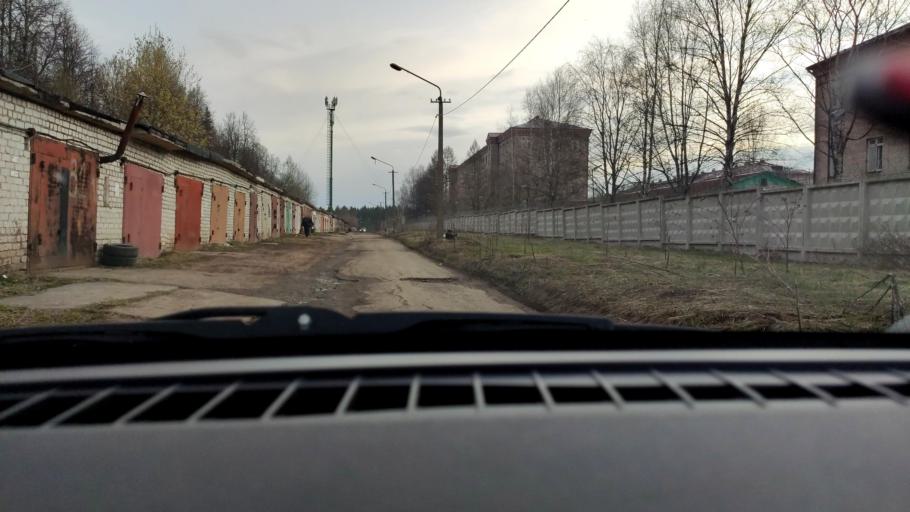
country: RU
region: Perm
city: Froly
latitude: 57.9716
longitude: 56.3208
